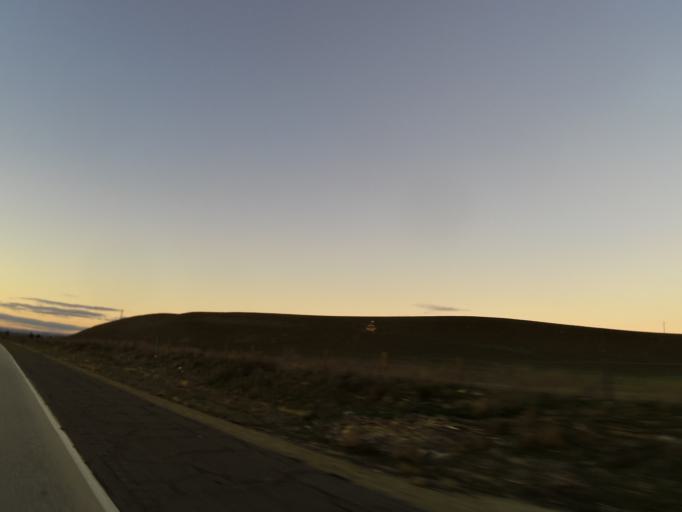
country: US
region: California
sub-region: Monterey County
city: King City
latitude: 36.1562
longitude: -121.0467
